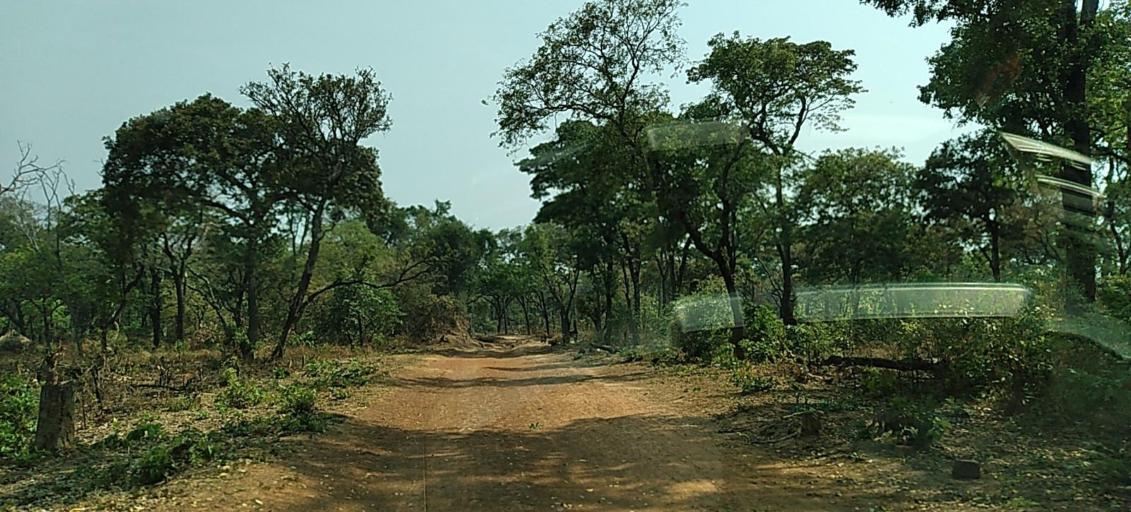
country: ZM
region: North-Western
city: Kansanshi
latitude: -12.0661
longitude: 26.8890
